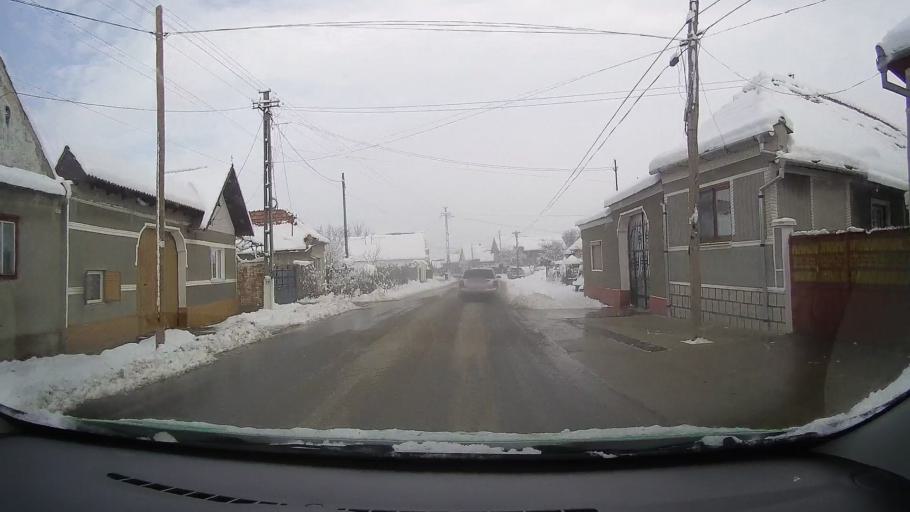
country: RO
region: Alba
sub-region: Comuna Pianu
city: Pianu de Jos
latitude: 45.9283
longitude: 23.4859
